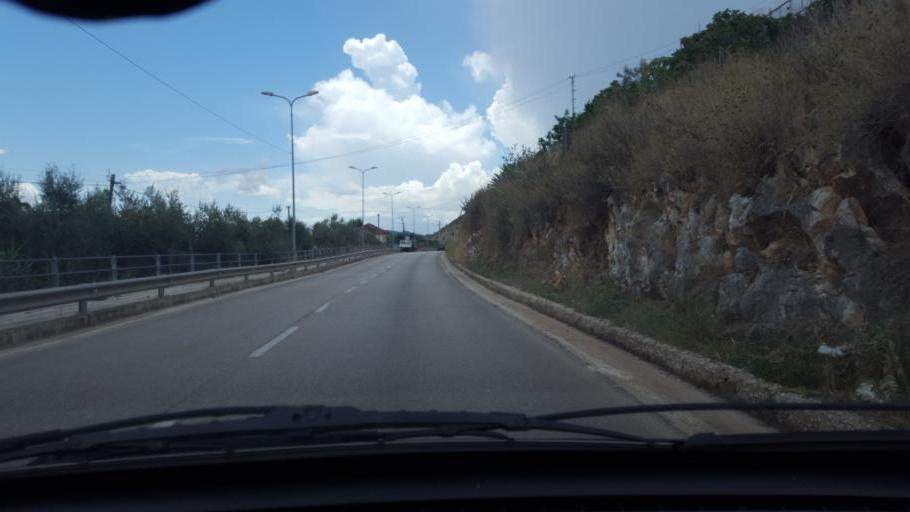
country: AL
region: Vlore
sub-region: Rrethi i Sarandes
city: Sarande
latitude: 39.8368
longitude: 20.0240
